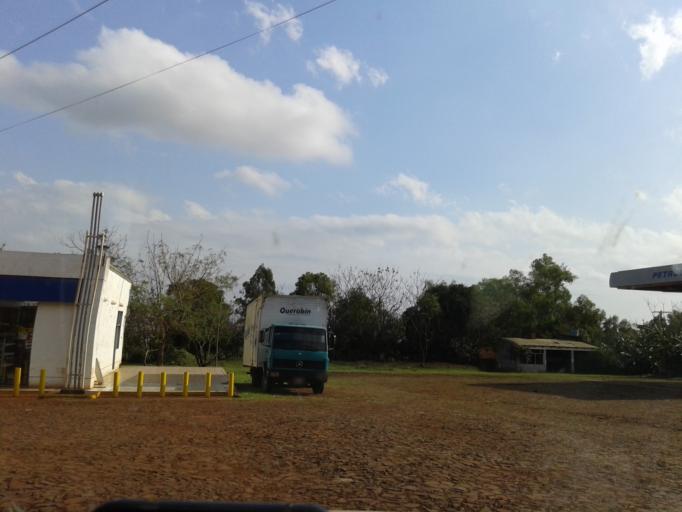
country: PY
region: Itapua
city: Arquitecto Tomas Romero Pereira
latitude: -26.5125
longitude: -55.2746
